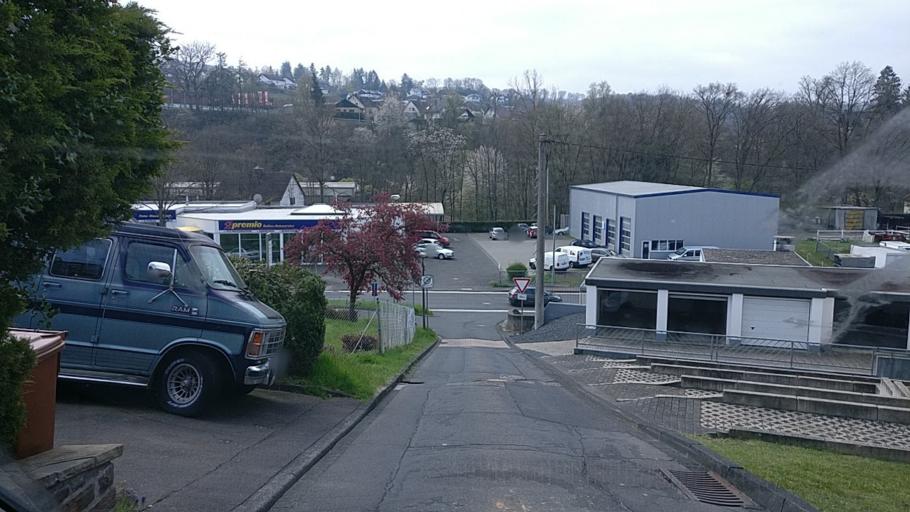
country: DE
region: Rheinland-Pfalz
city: Peterslahr
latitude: 50.6257
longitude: 7.4315
